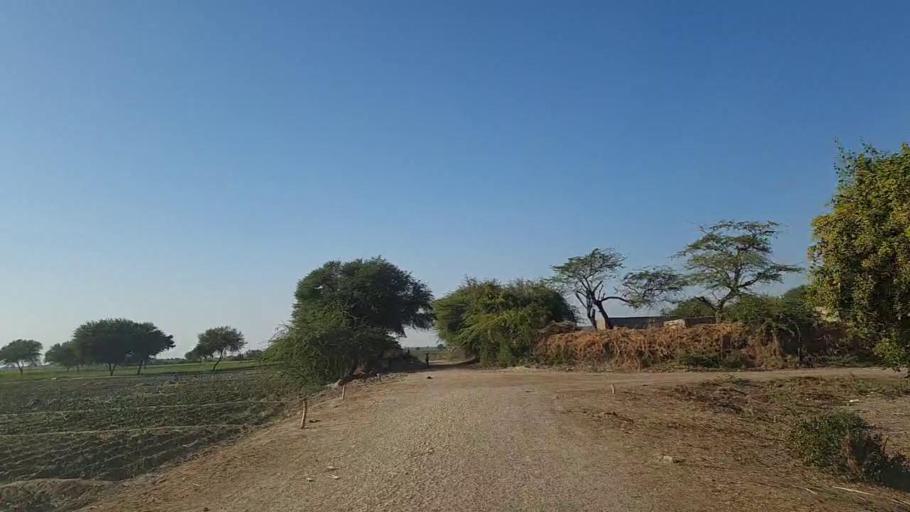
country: PK
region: Sindh
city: Naukot
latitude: 24.9697
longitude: 69.3475
